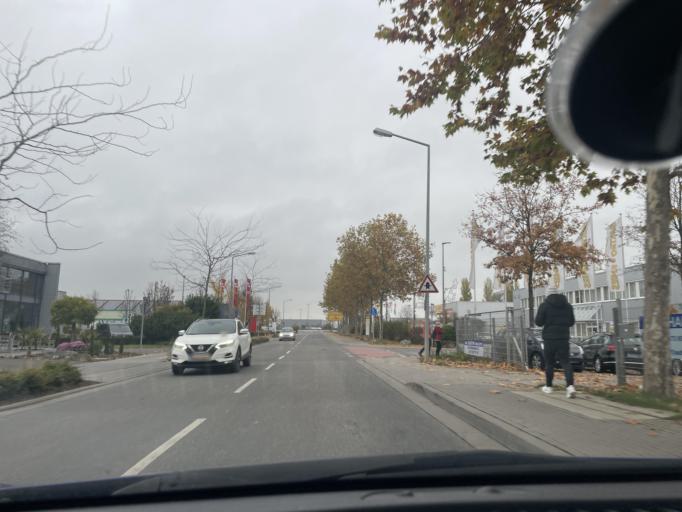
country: DE
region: Rheinland-Pfalz
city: Worms
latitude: 49.6571
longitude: 8.3541
